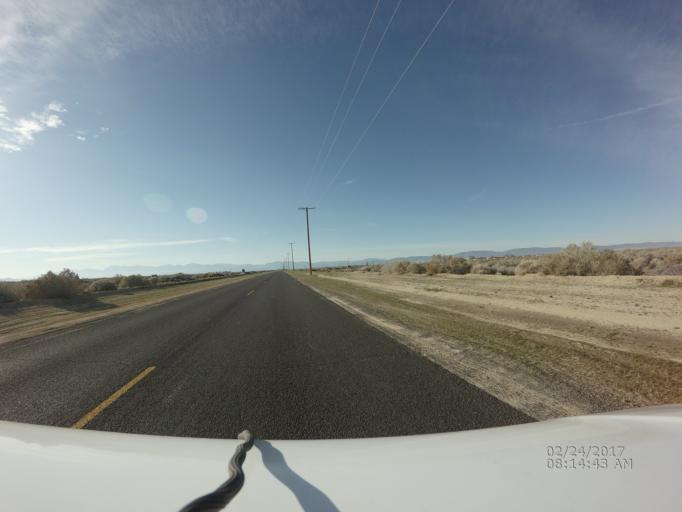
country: US
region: California
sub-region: Los Angeles County
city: Lancaster
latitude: 34.7396
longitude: -118.0412
